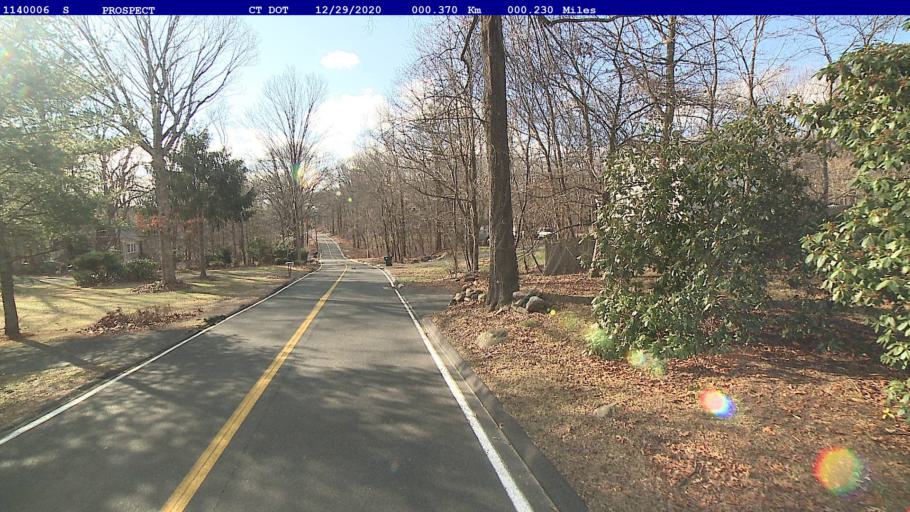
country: US
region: Connecticut
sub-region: New Haven County
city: Prospect
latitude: 41.5140
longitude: -73.0041
